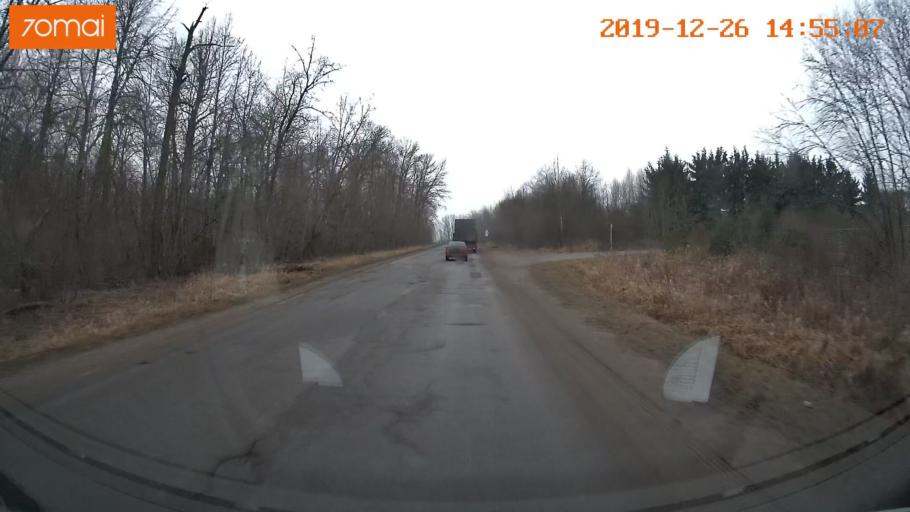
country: RU
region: Jaroslavl
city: Rybinsk
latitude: 58.3026
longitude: 38.8777
